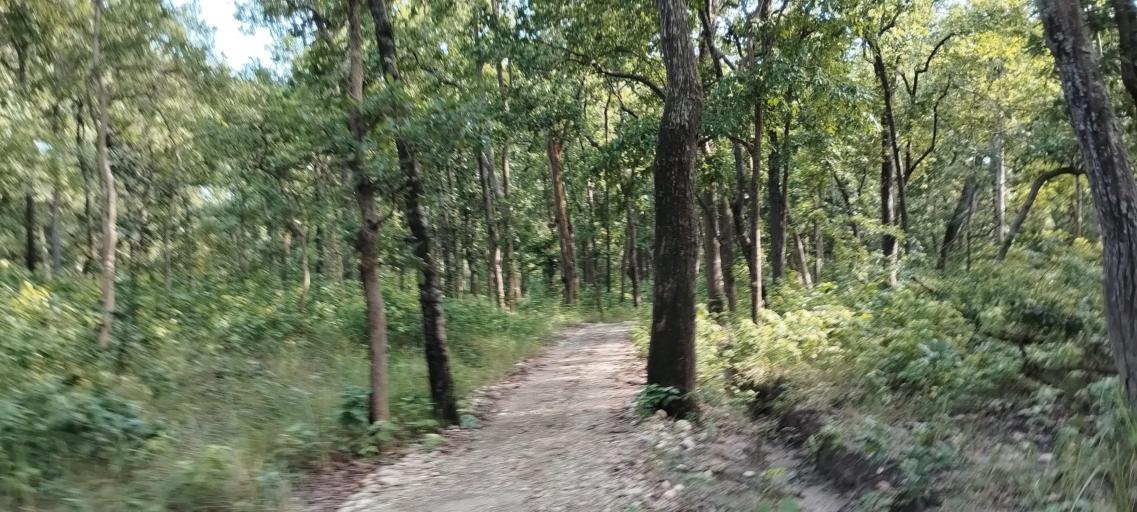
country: NP
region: Far Western
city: Tikapur
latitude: 28.5580
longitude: 81.2667
